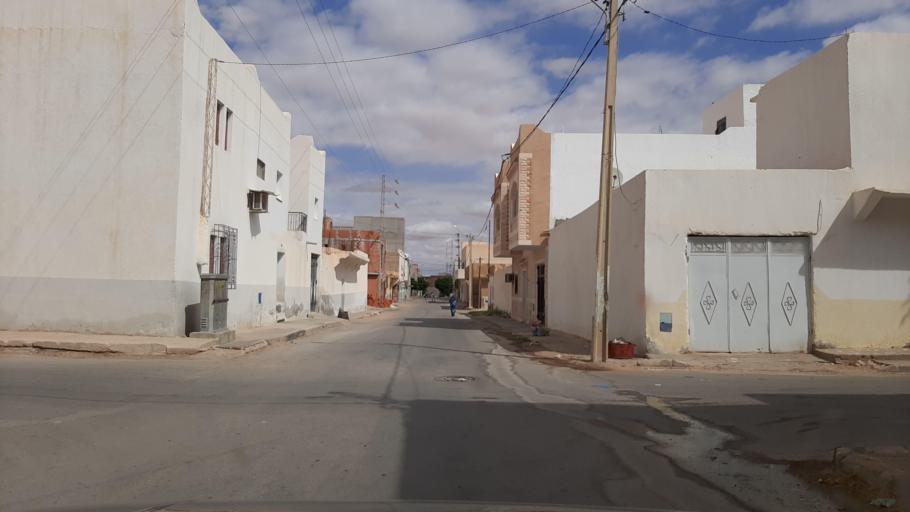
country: TN
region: Tataouine
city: Tataouine
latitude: 32.9272
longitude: 10.4561
